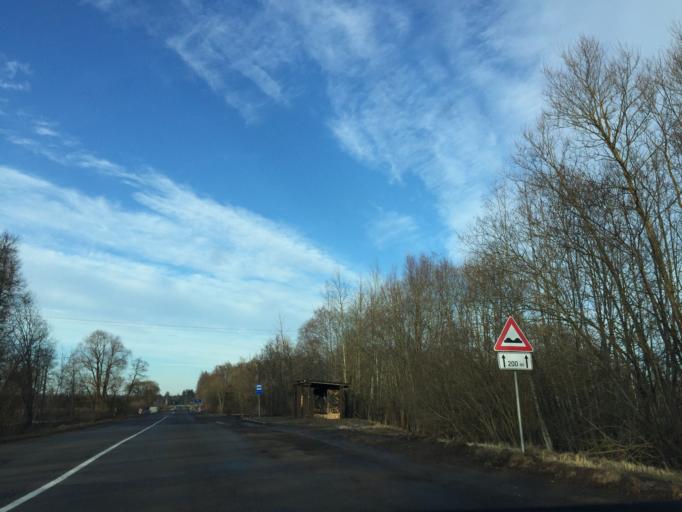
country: LV
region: Kekava
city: Balozi
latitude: 56.7668
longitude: 24.1088
